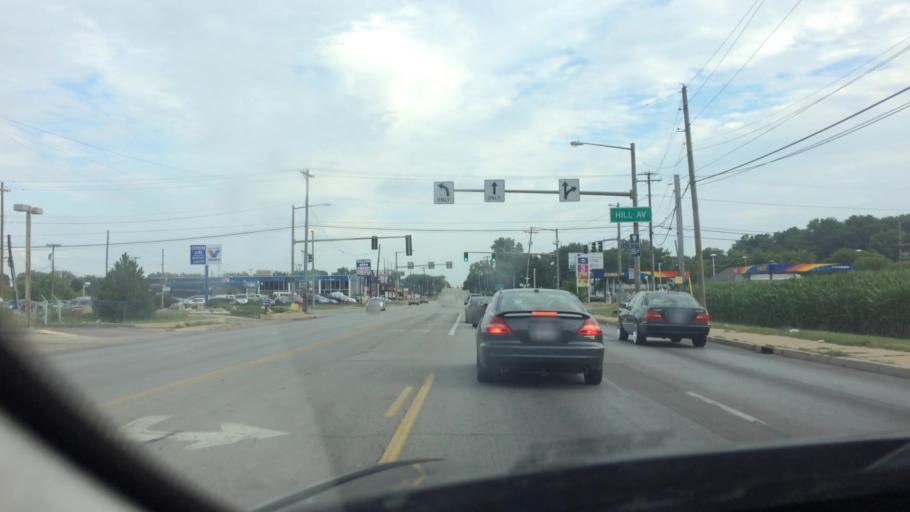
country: US
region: Ohio
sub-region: Lucas County
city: Ottawa Hills
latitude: 41.6390
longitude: -83.6260
